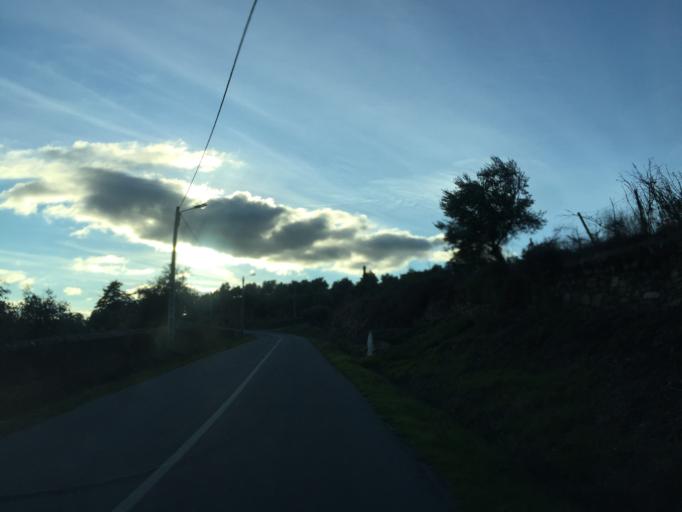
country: PT
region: Portalegre
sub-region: Alter do Chao
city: Alter do Chao
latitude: 39.2829
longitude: -7.6415
